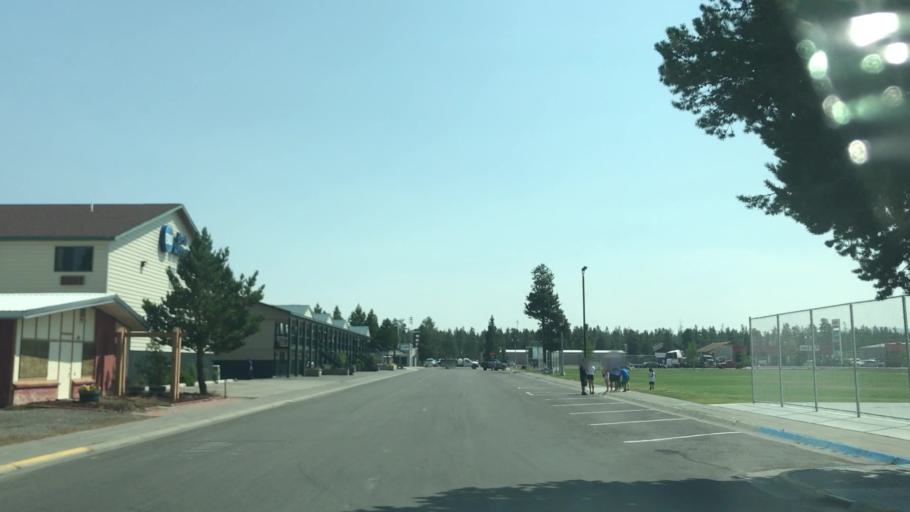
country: US
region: Montana
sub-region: Gallatin County
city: West Yellowstone
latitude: 44.6639
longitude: -111.1019
